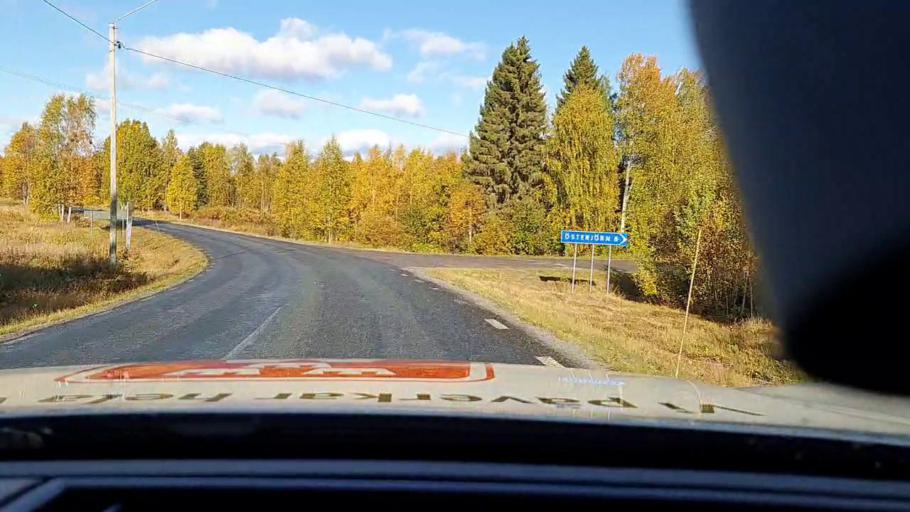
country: SE
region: Vaesterbotten
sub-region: Skelleftea Kommun
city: Langsele
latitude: 65.0046
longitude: 20.0909
